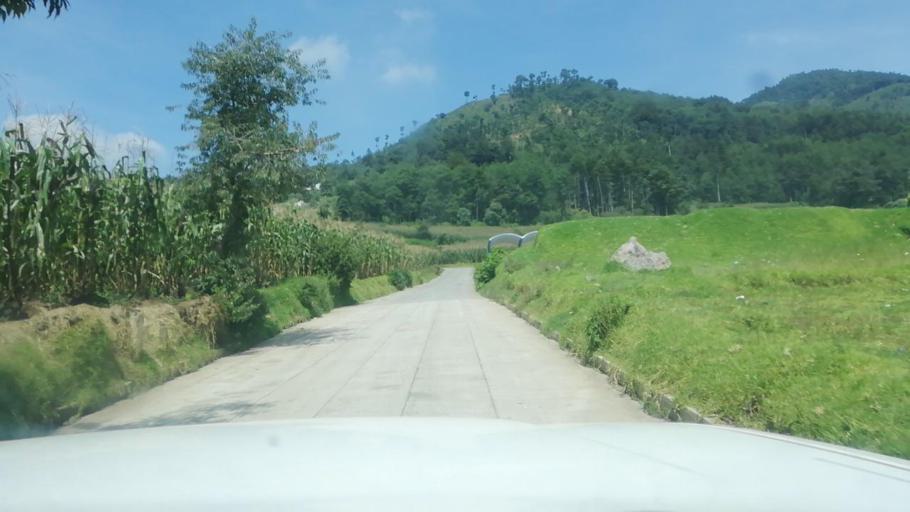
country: GT
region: Totonicapan
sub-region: Municipio de San Andres Xecul
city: San Andres Xecul
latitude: 14.8937
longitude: -91.4763
